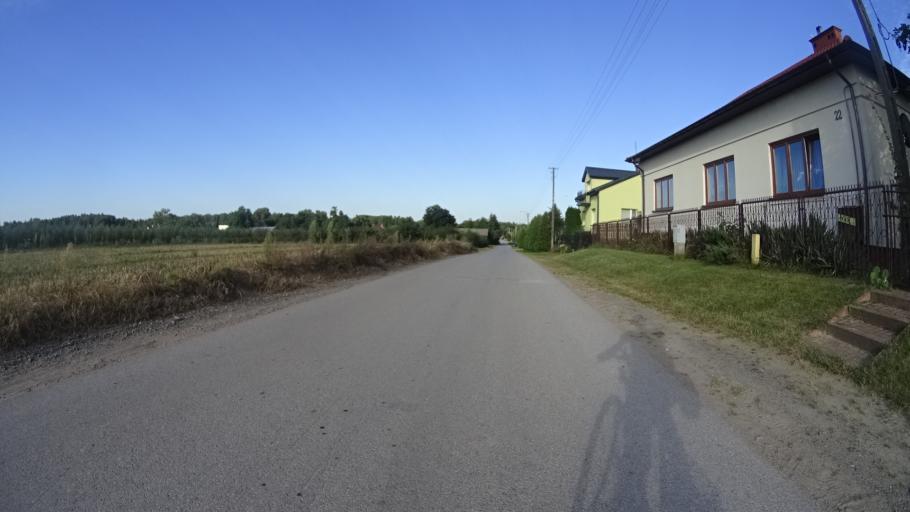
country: PL
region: Masovian Voivodeship
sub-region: Powiat grojecki
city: Goszczyn
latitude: 51.6926
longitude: 20.8116
